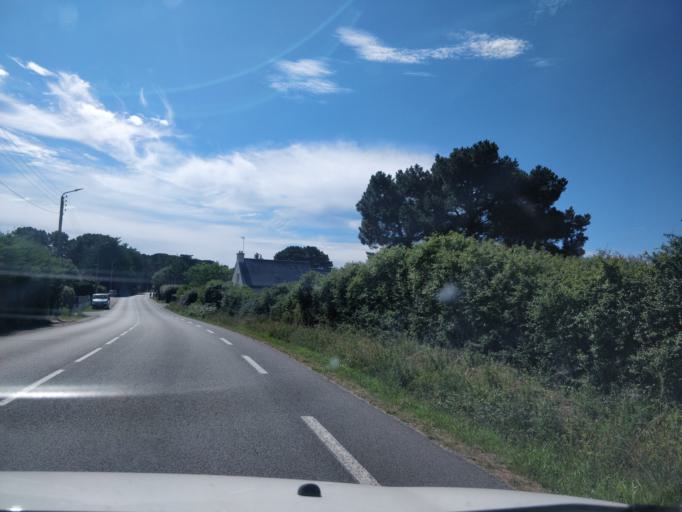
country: FR
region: Brittany
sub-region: Departement du Morbihan
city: Saint-Philibert
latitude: 47.5741
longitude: -3.0004
